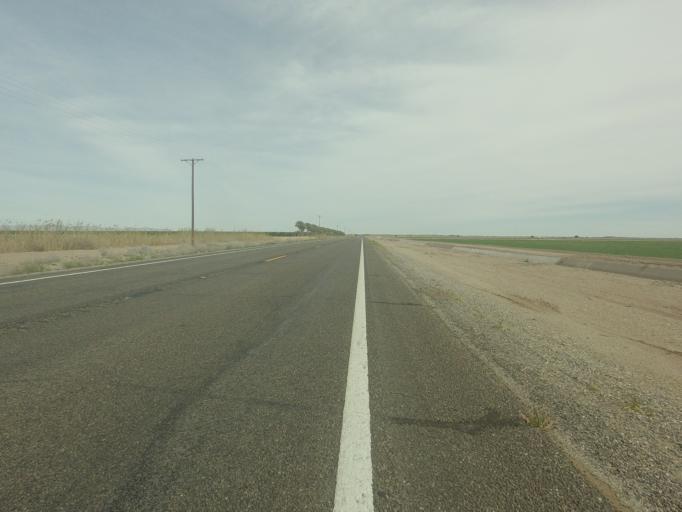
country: US
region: California
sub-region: Imperial County
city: Holtville
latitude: 32.9748
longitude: -115.3182
